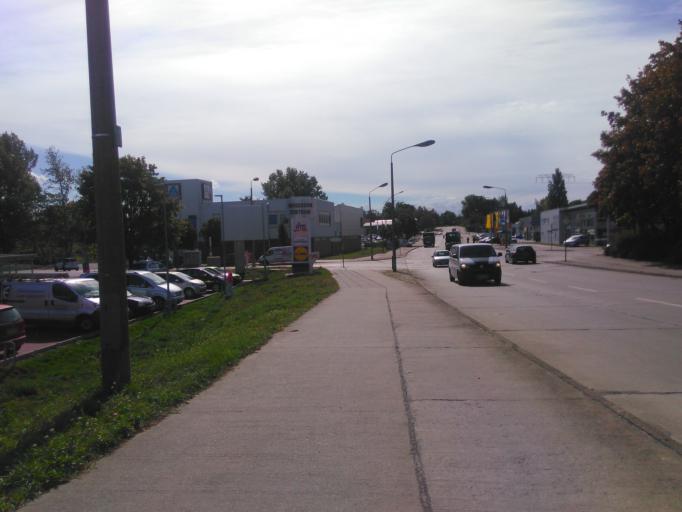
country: DE
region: Berlin
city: Altglienicke
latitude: 52.4252
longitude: 13.5267
